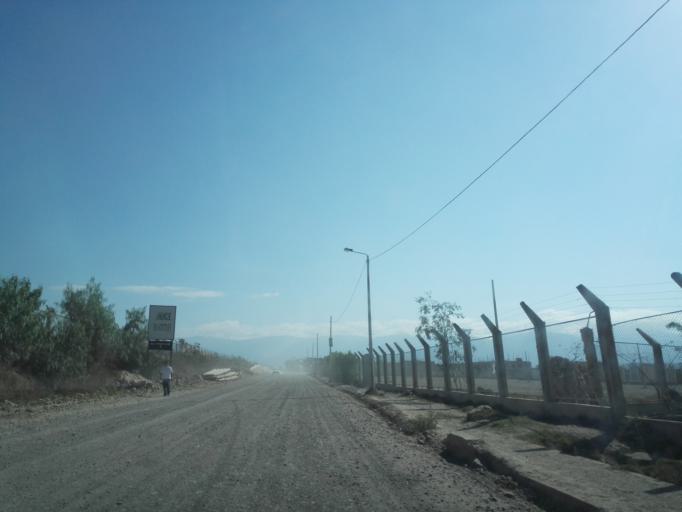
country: PE
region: Ayacucho
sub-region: Provincia de Huamanga
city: Ayacucho
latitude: -13.1612
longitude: -74.2065
